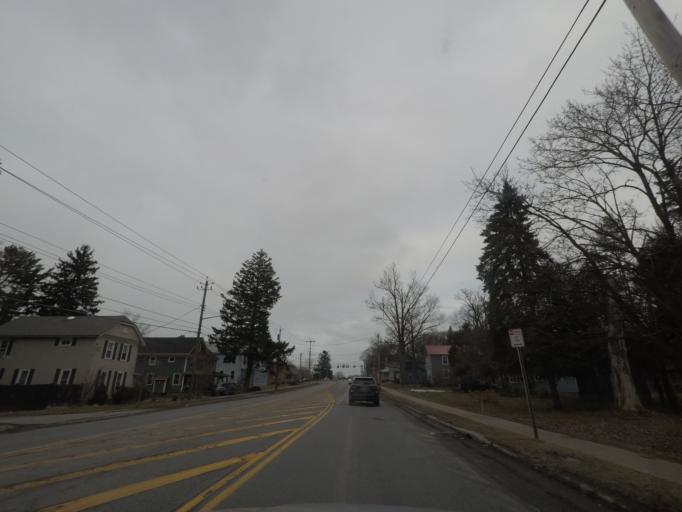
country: US
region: New York
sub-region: Madison County
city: Wampsville
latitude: 43.0751
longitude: -75.7085
